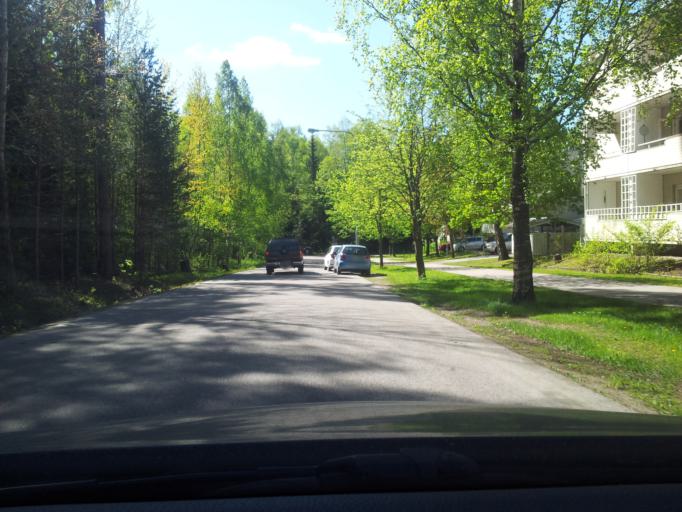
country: FI
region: Uusimaa
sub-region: Helsinki
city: Kauniainen
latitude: 60.1732
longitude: 24.7110
